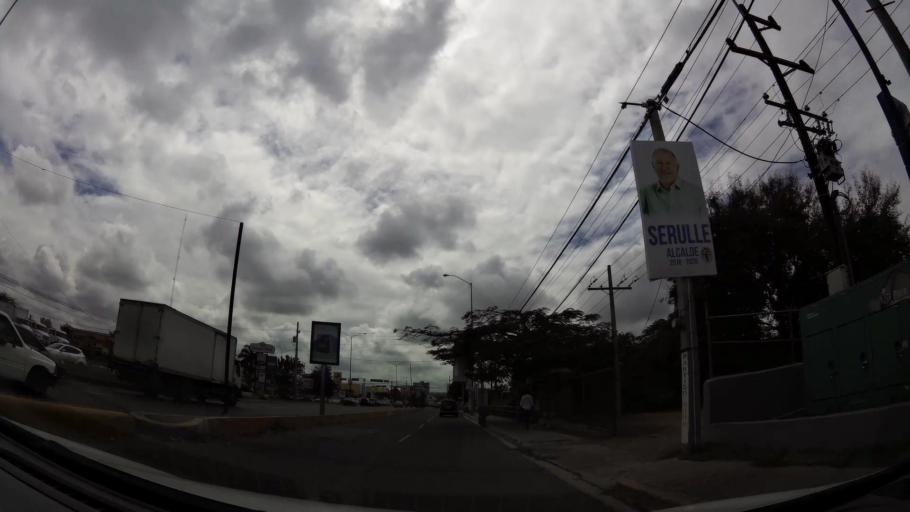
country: DO
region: Santiago
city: Santiago de los Caballeros
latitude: 19.4453
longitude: -70.6727
